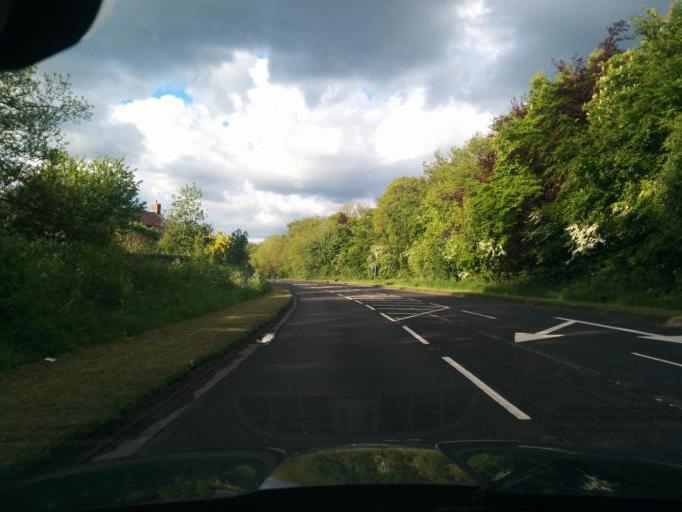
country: GB
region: England
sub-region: Northumberland
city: Bedlington
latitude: 55.1178
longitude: -1.6174
